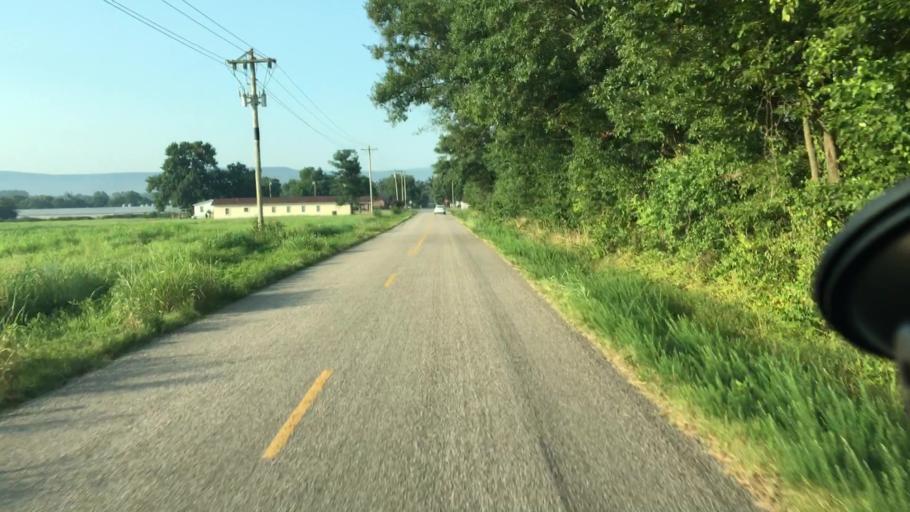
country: US
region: Arkansas
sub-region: Johnson County
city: Coal Hill
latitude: 35.3394
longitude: -93.6138
